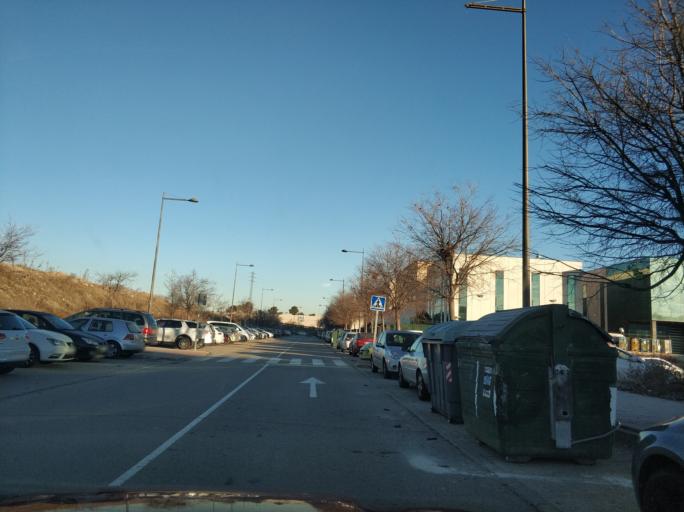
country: ES
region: Madrid
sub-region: Provincia de Madrid
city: Getafe
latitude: 40.2923
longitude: -3.7043
